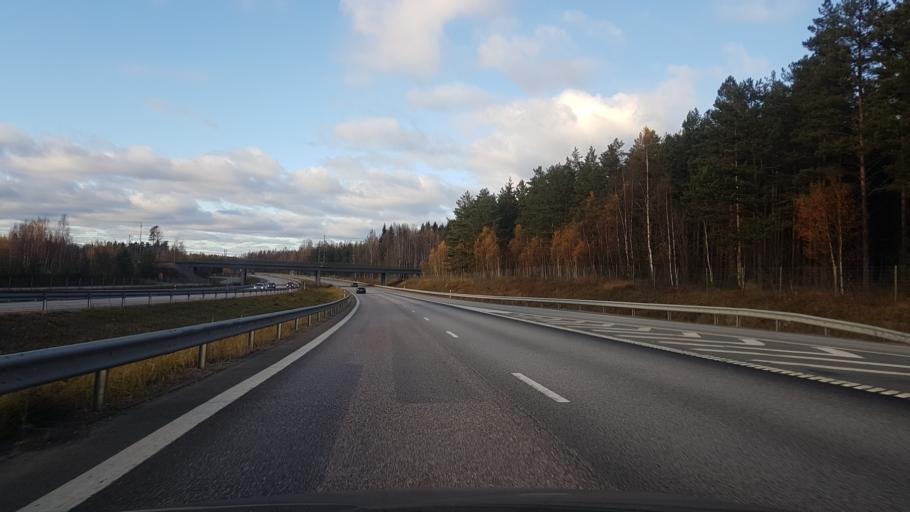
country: SE
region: Uppsala
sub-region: Alvkarleby Kommun
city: AElvkarleby
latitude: 60.4654
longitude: 17.4105
